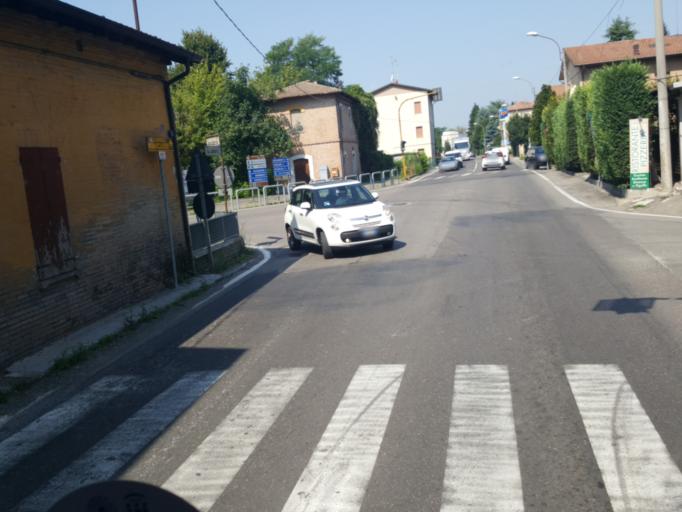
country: IT
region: Emilia-Romagna
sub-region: Provincia di Modena
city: Ca' di Sola
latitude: 44.5420
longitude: 10.9566
